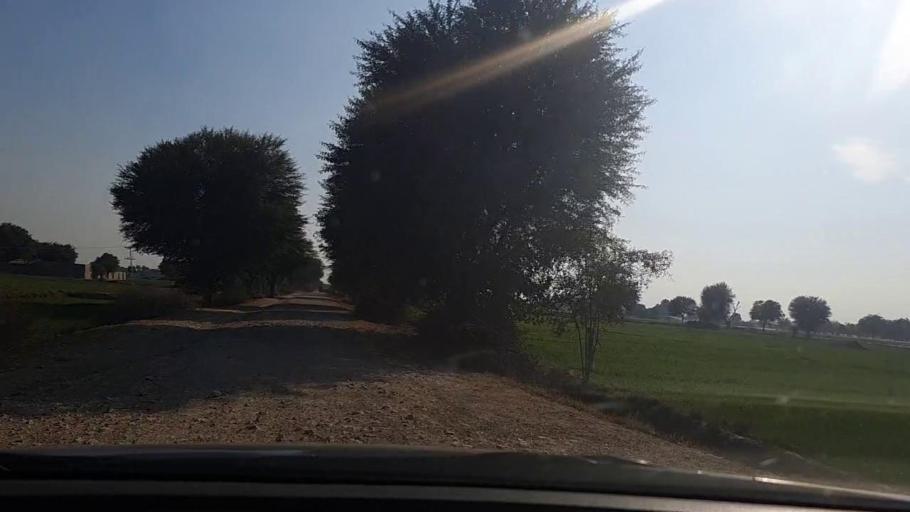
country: PK
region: Sindh
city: Sehwan
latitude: 26.3194
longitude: 68.0062
